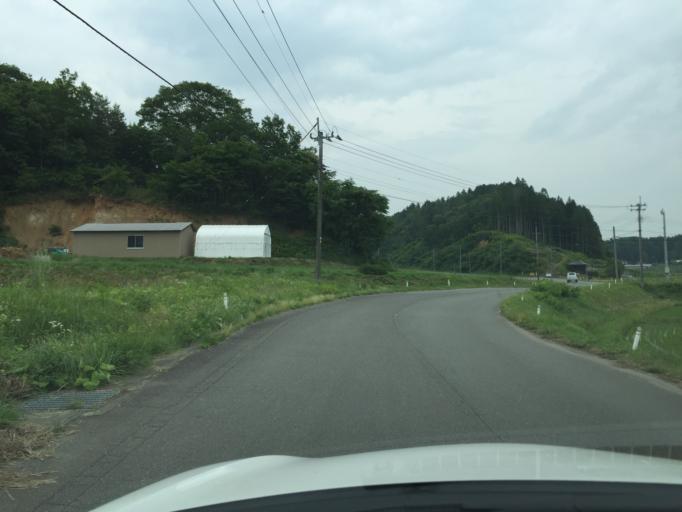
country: JP
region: Fukushima
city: Iwaki
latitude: 37.1896
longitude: 140.7189
